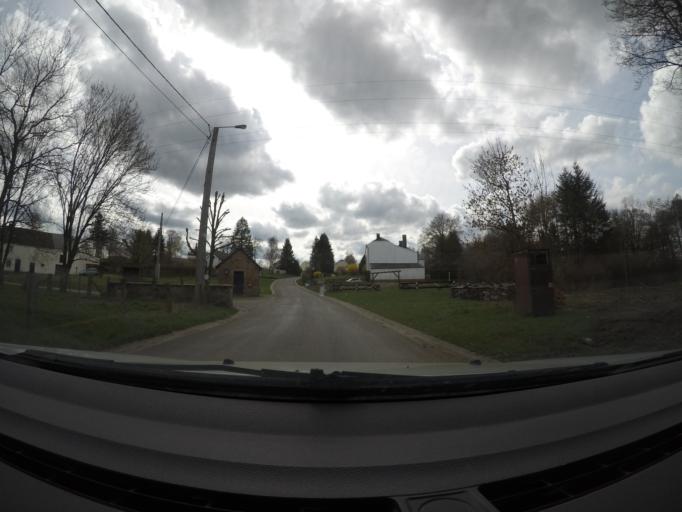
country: BE
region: Wallonia
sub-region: Province du Luxembourg
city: Leglise
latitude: 49.7999
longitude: 5.4857
